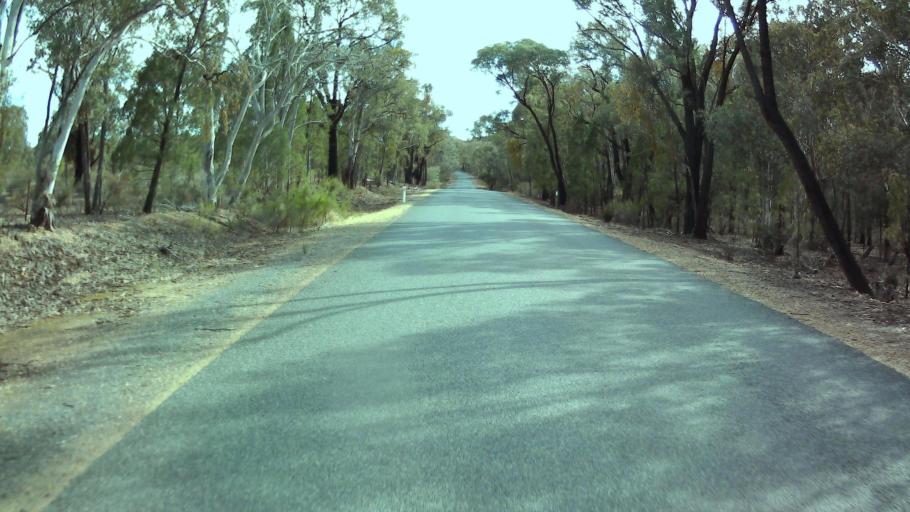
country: AU
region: New South Wales
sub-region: Weddin
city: Grenfell
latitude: -33.8866
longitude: 148.1968
